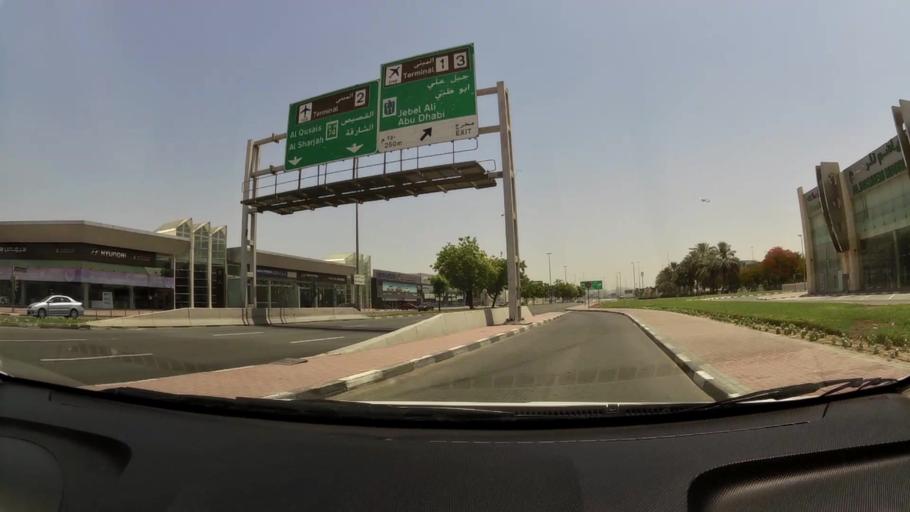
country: AE
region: Ash Shariqah
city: Sharjah
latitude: 25.2612
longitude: 55.3341
